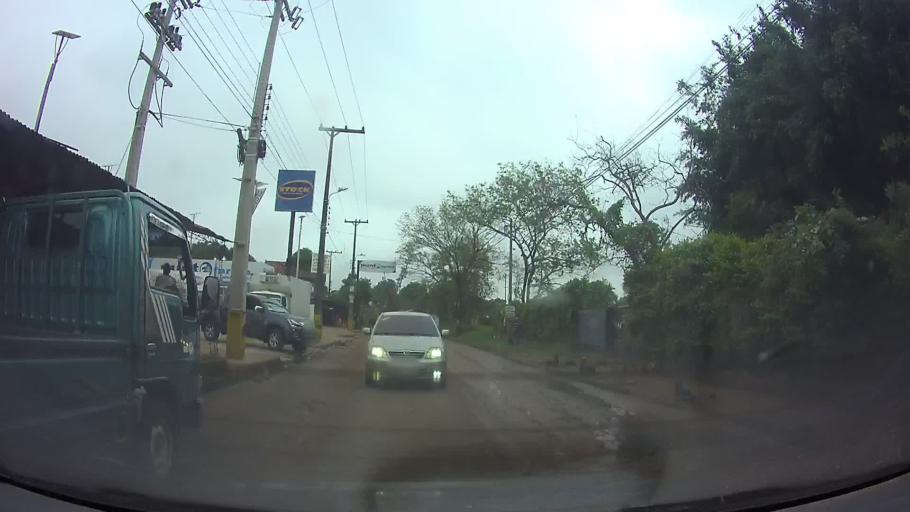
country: PY
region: Central
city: San Lorenzo
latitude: -25.3142
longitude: -57.4934
